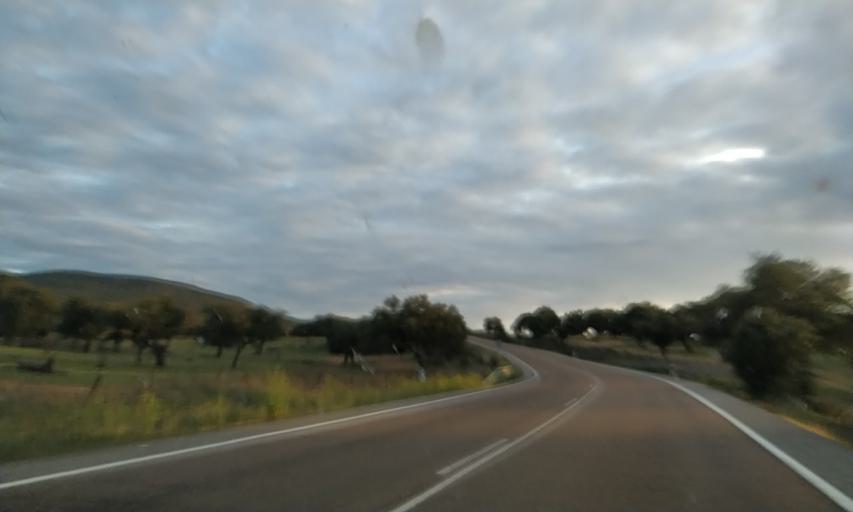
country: ES
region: Extremadura
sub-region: Provincia de Badajoz
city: Puebla de Obando
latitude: 39.2148
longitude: -6.5823
